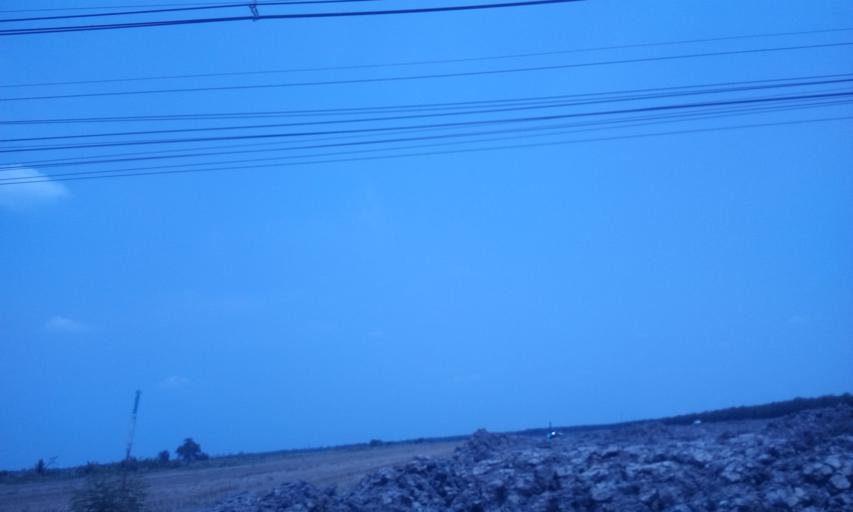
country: TH
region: Bangkok
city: Nong Chok
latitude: 13.9687
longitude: 100.9471
